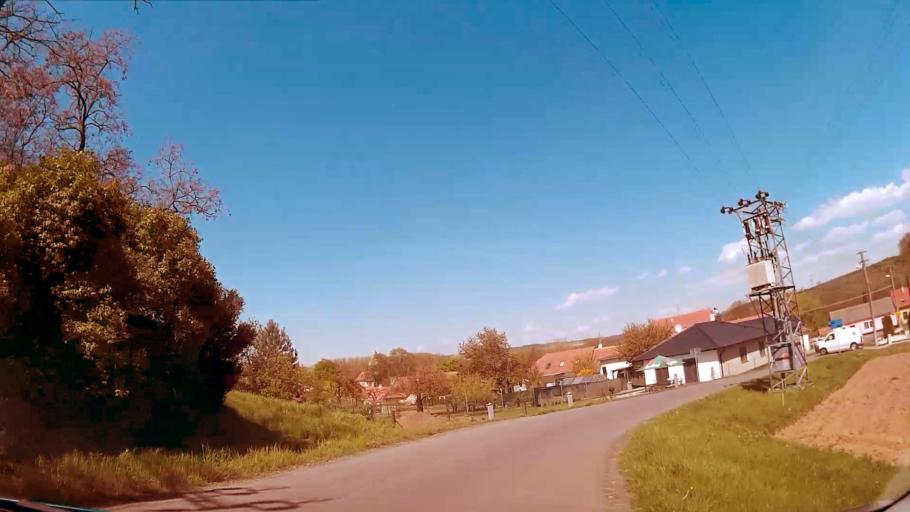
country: CZ
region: South Moravian
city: Moravsky Krumlov
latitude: 49.0838
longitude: 16.3200
